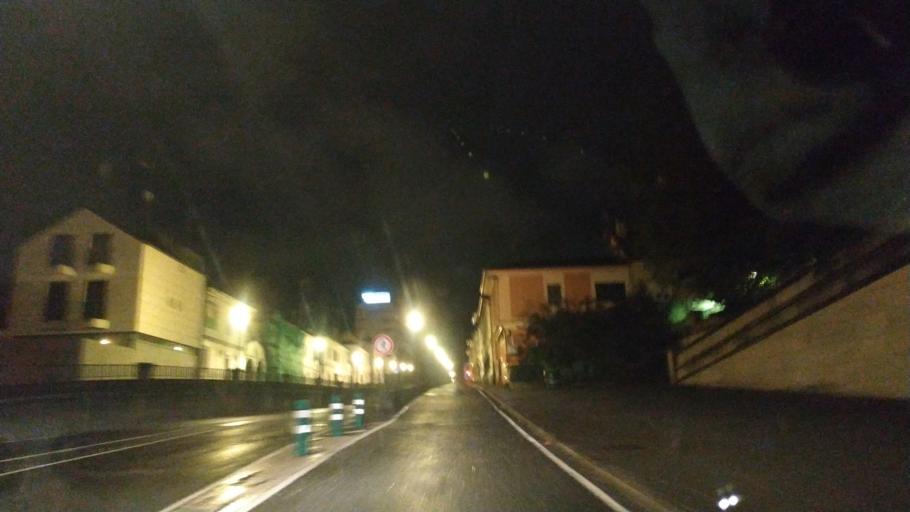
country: ES
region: Galicia
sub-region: Provincia da Coruna
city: A Coruna
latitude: 43.3608
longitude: -8.4111
